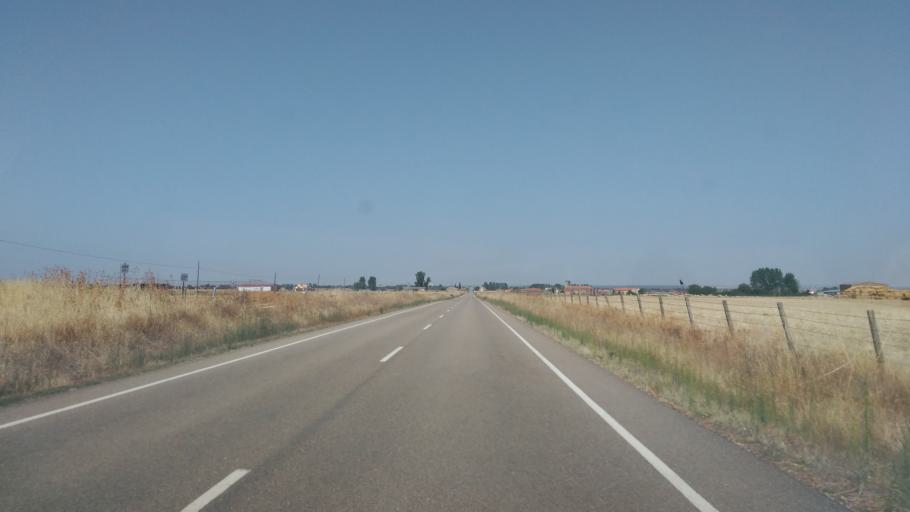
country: ES
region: Castille and Leon
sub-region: Provincia de Salamanca
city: La Fuente de San Esteban
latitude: 40.7705
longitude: -6.2233
